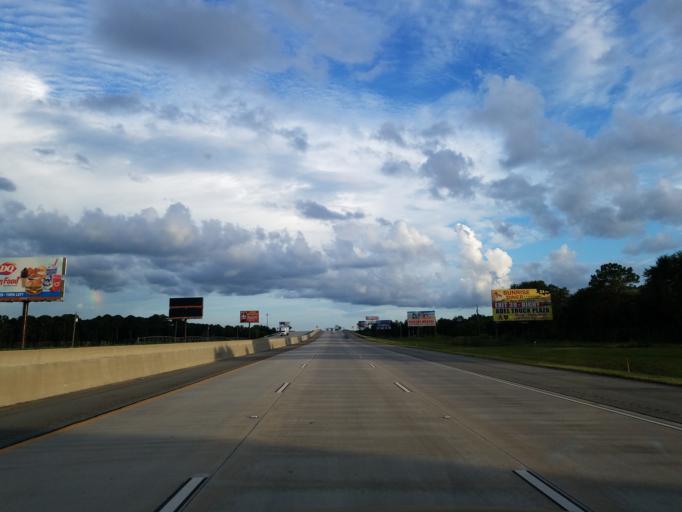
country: US
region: Georgia
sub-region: Cook County
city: Sparks
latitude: 31.1830
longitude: -83.4521
